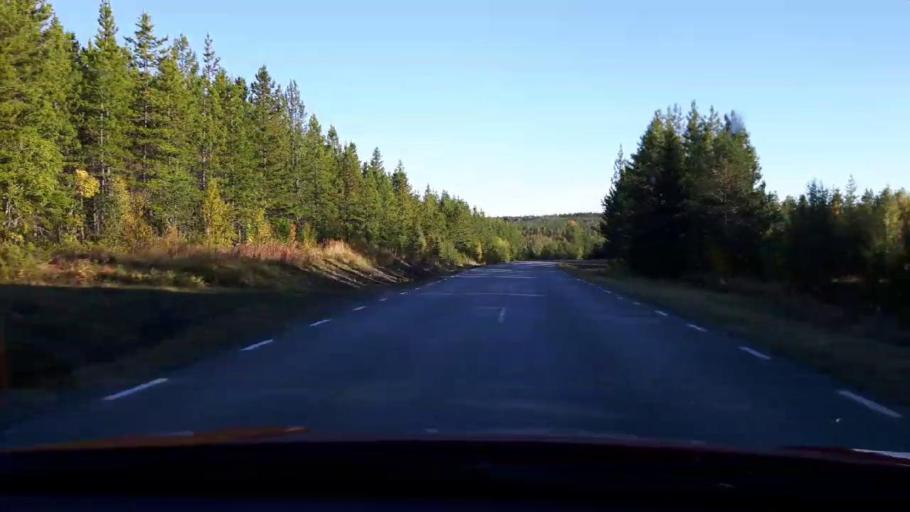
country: SE
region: Jaemtland
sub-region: OEstersunds Kommun
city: Lit
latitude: 63.7699
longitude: 14.7194
